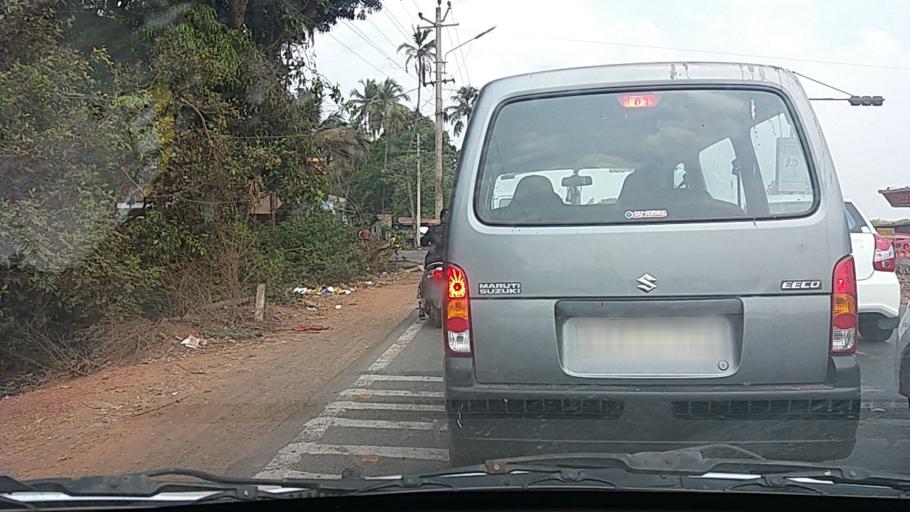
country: IN
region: Goa
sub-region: North Goa
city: Bambolim
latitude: 15.4783
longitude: 73.8485
